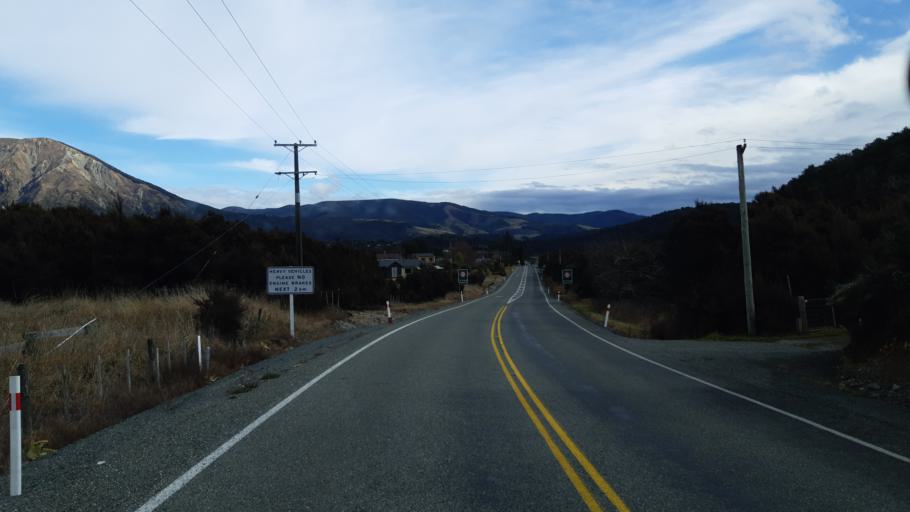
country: NZ
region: Tasman
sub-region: Tasman District
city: Wakefield
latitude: -41.8005
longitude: 172.8595
